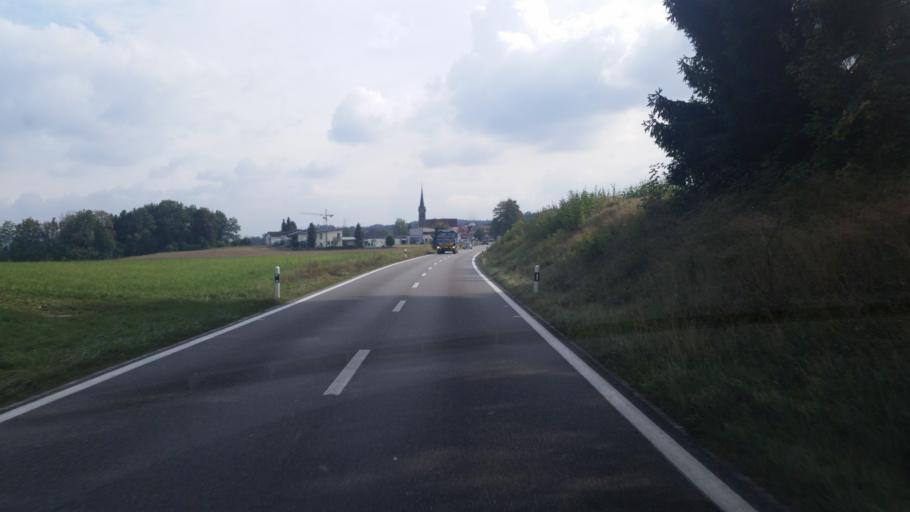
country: CH
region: Aargau
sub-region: Bezirk Baden
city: Kunten
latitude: 47.3783
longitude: 8.3017
